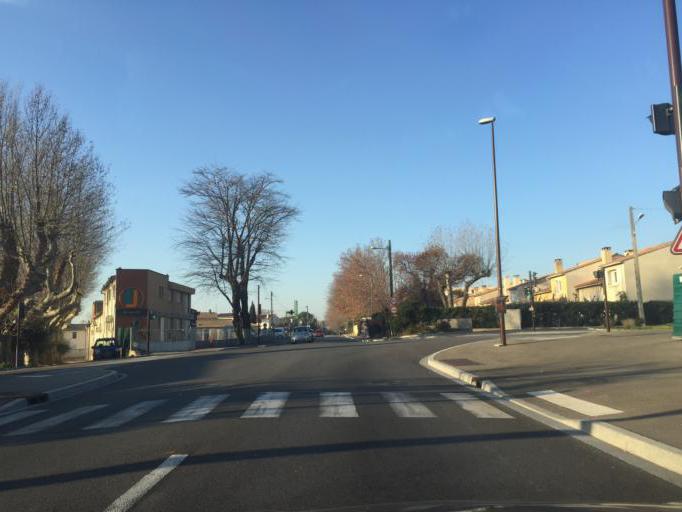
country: FR
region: Provence-Alpes-Cote d'Azur
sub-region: Departement du Vaucluse
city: Montfavet
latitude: 43.9288
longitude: 4.8761
